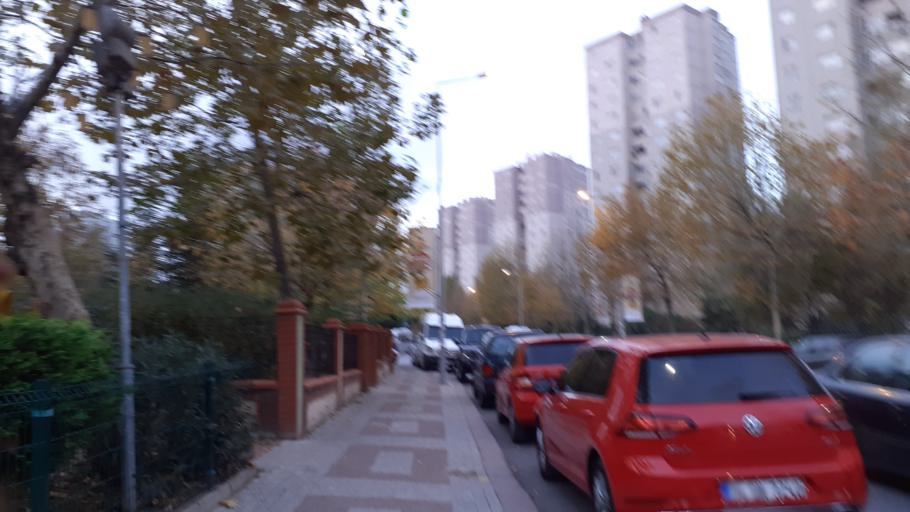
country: TR
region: Istanbul
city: Mahmutbey
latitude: 41.0569
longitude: 28.7899
